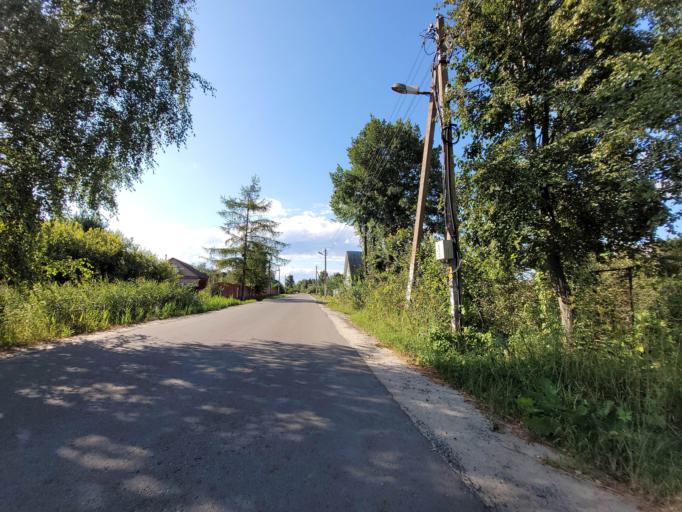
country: RU
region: Moskovskaya
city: Konobeyevo
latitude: 55.4071
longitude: 38.7031
